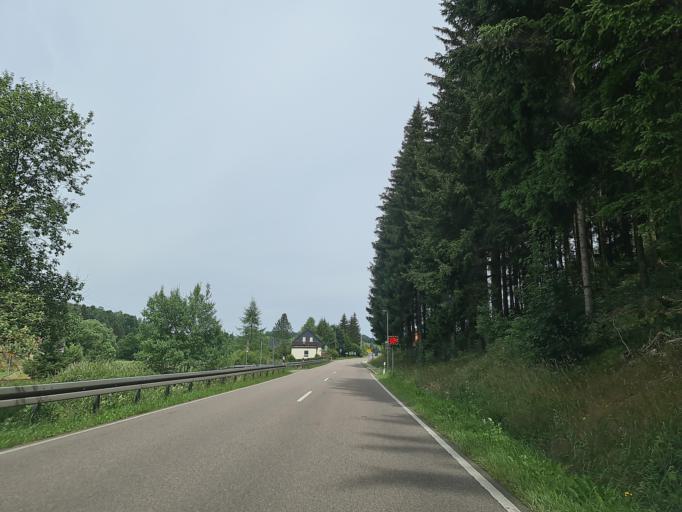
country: DE
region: Saxony
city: Heidersdorf
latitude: 50.6568
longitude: 13.4060
